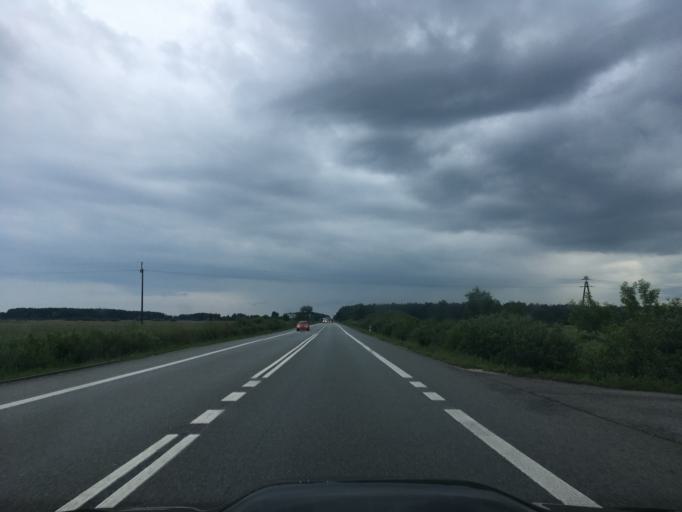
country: PL
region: Masovian Voivodeship
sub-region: Powiat otwocki
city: Celestynow
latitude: 52.0322
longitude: 21.3221
